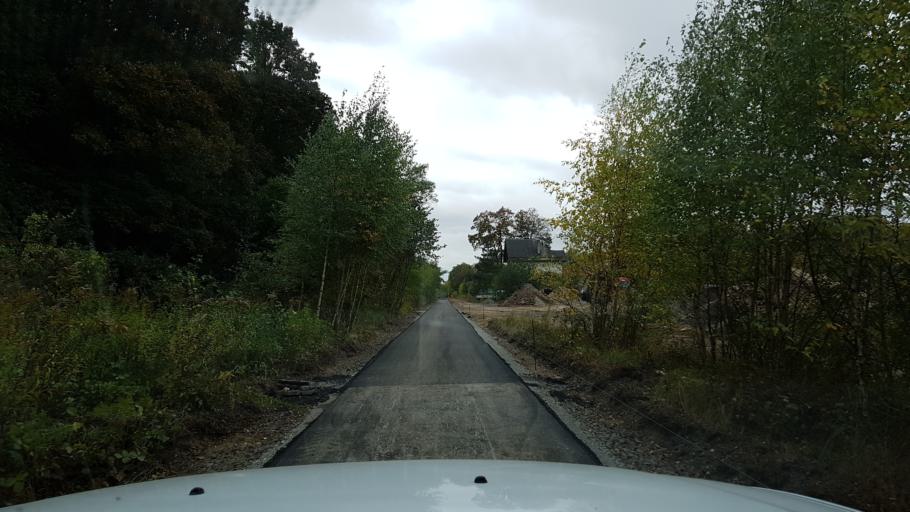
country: PL
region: West Pomeranian Voivodeship
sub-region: Powiat gryfinski
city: Cedynia
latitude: 52.8224
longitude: 14.2367
